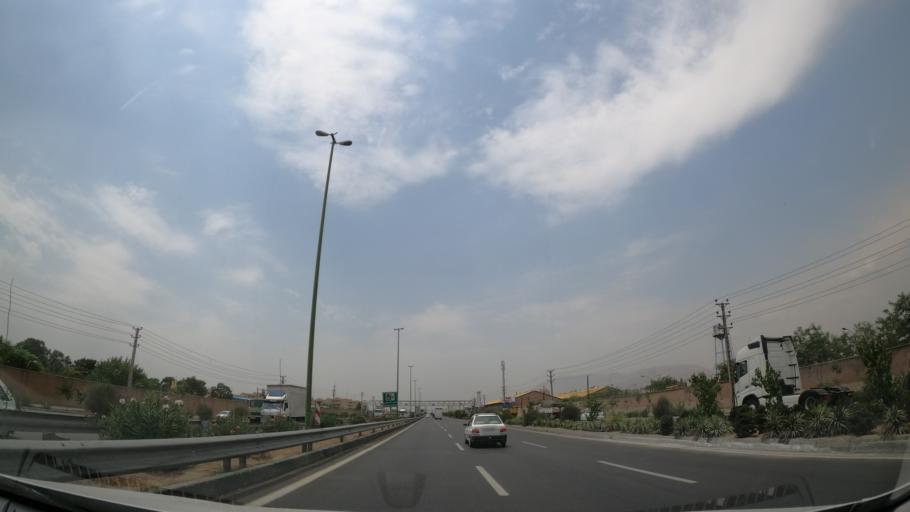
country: IR
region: Tehran
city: Shahr-e Qods
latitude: 35.6949
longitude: 51.2051
